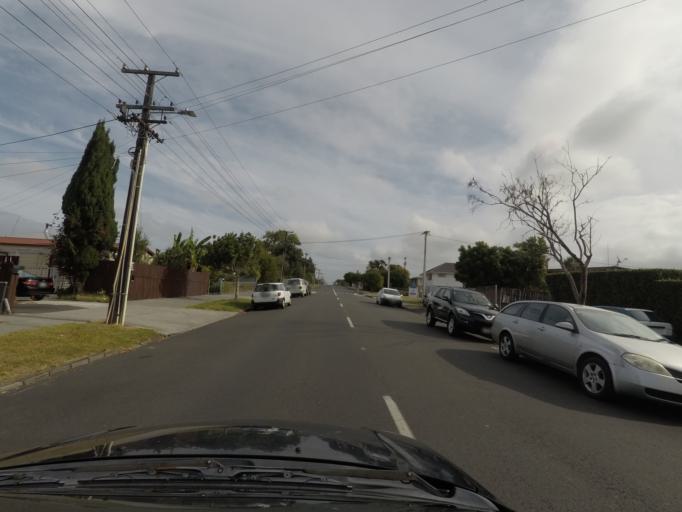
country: NZ
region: Auckland
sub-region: Auckland
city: Waitakere
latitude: -36.9019
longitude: 174.6657
